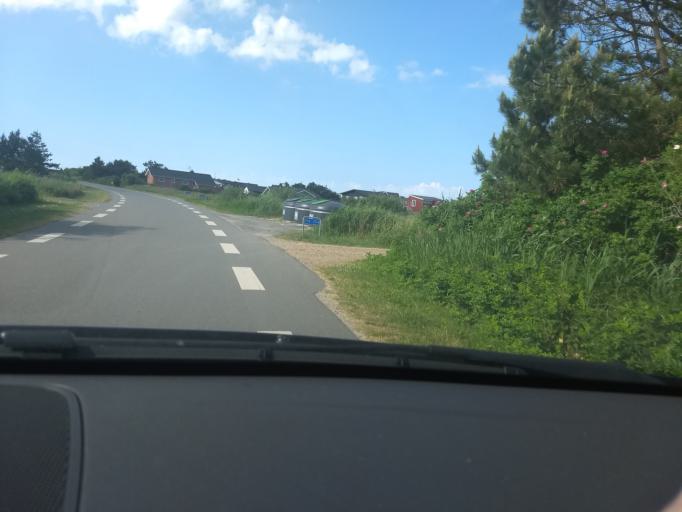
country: DE
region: Schleswig-Holstein
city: List
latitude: 55.1378
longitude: 8.4933
